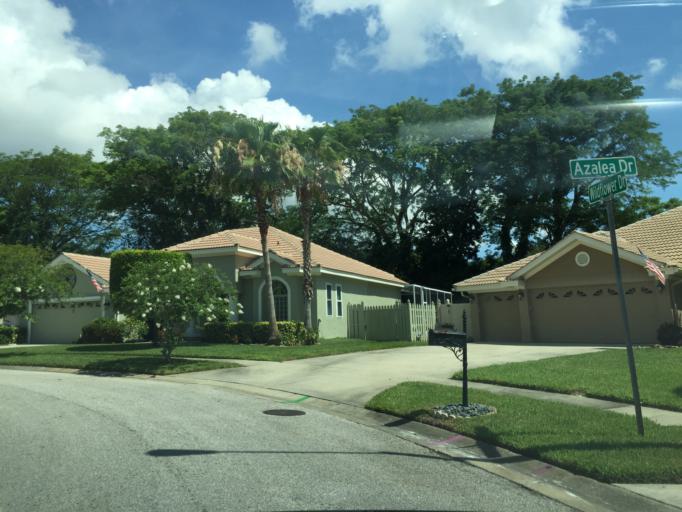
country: US
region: Florida
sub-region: Pinellas County
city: Saint George
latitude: 28.0582
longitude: -82.7415
